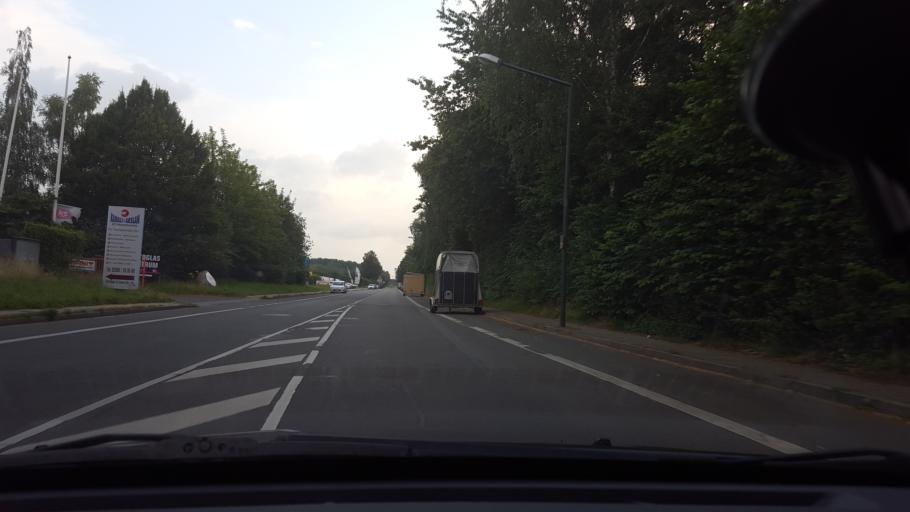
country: DE
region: North Rhine-Westphalia
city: Herten
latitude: 51.6059
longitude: 7.1053
